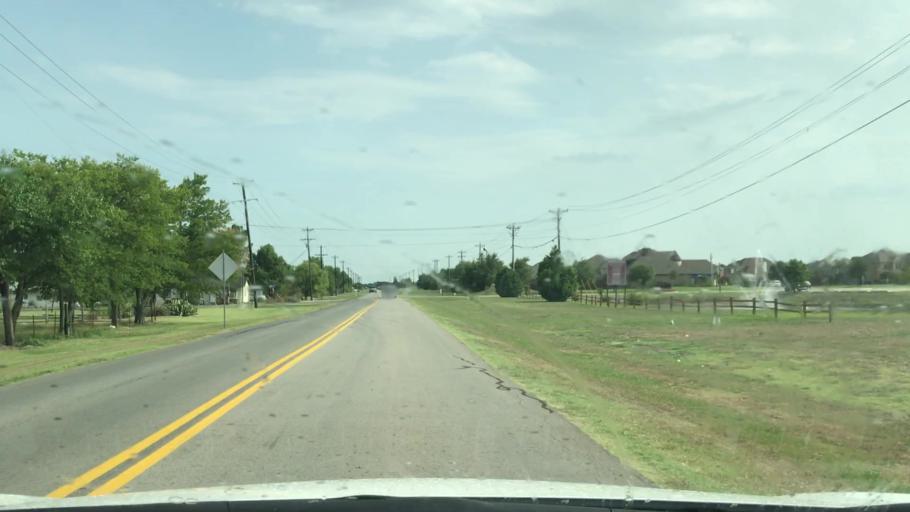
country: US
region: Texas
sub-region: Collin County
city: Wylie
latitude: 32.9904
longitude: -96.5217
